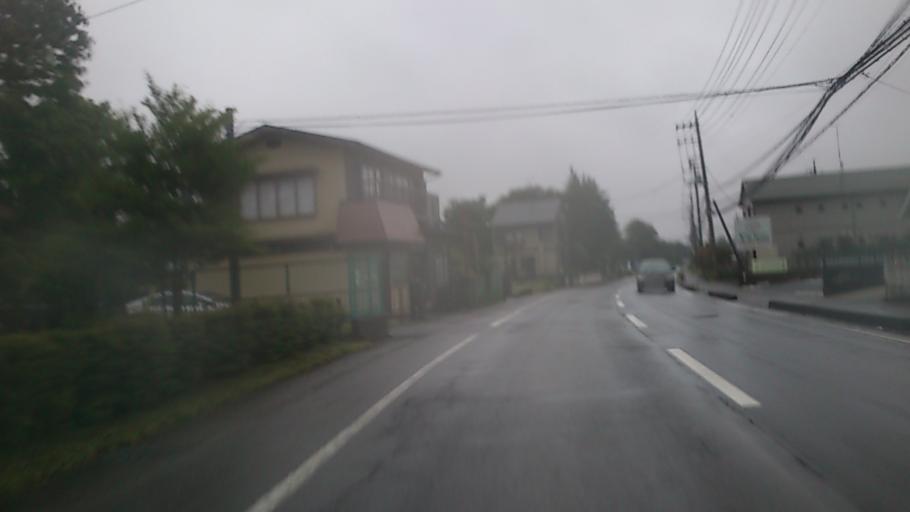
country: JP
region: Tochigi
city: Otawara
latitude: 36.9119
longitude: 139.9806
